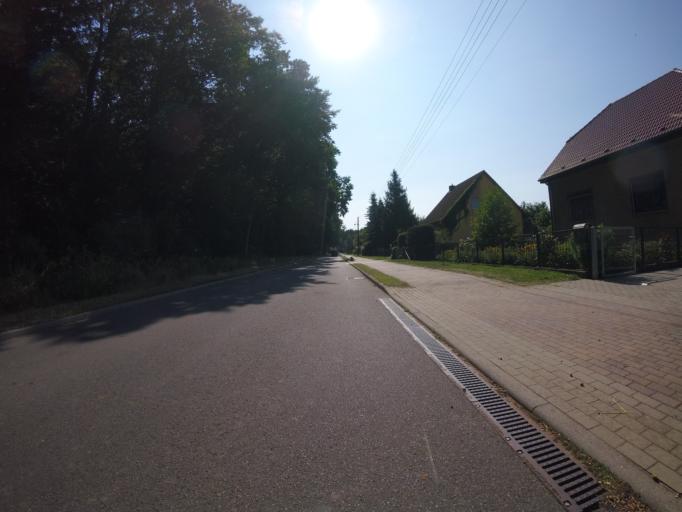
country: DE
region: Brandenburg
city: Mullrose
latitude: 52.2618
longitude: 14.3757
